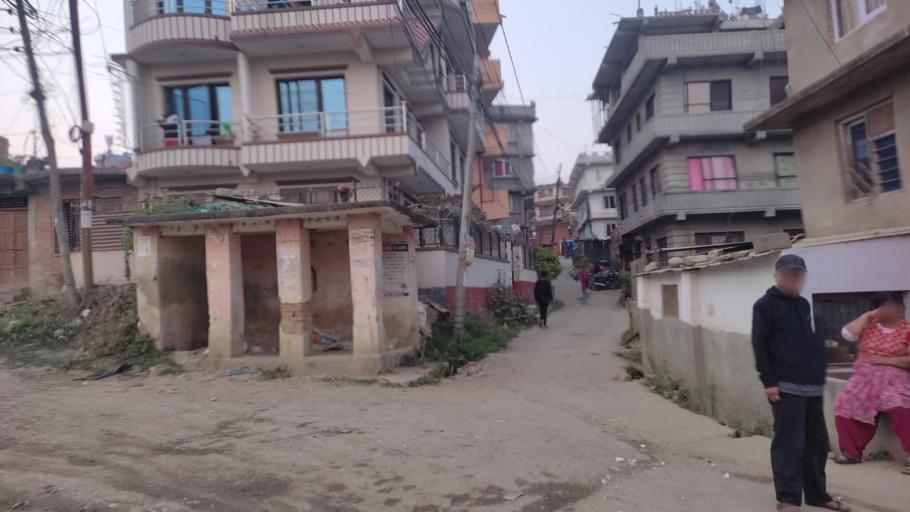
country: NP
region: Central Region
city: Kirtipur
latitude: 27.6680
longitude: 85.2786
